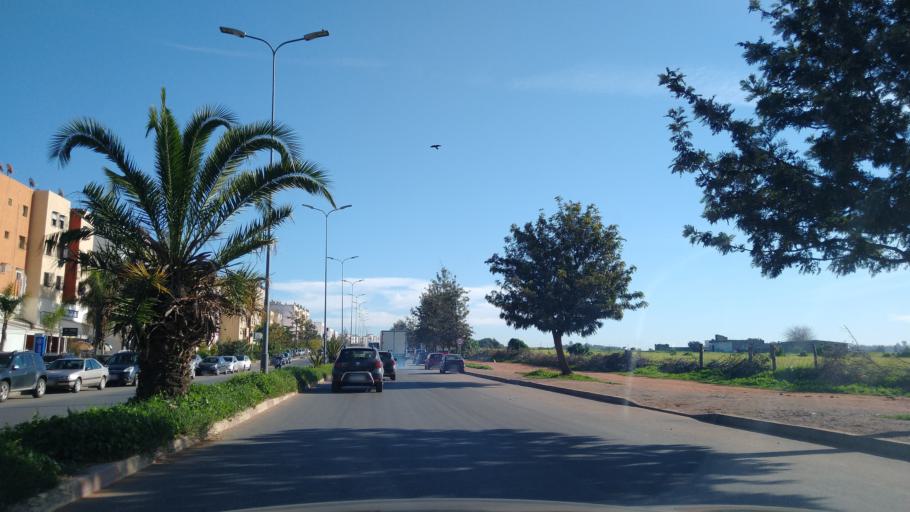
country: MA
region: Rabat-Sale-Zemmour-Zaer
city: Sale
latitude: 33.9932
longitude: -6.7439
